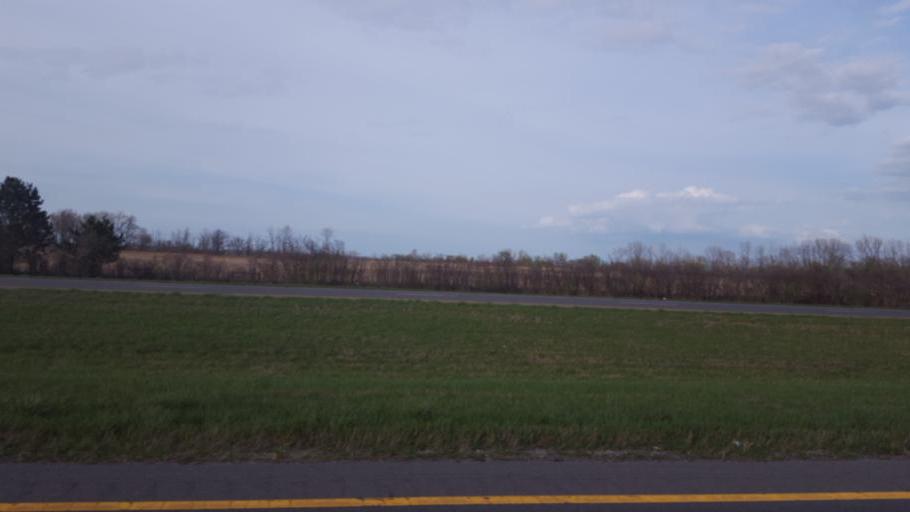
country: US
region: Ohio
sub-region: Erie County
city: Sandusky
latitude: 41.4505
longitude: -82.7942
